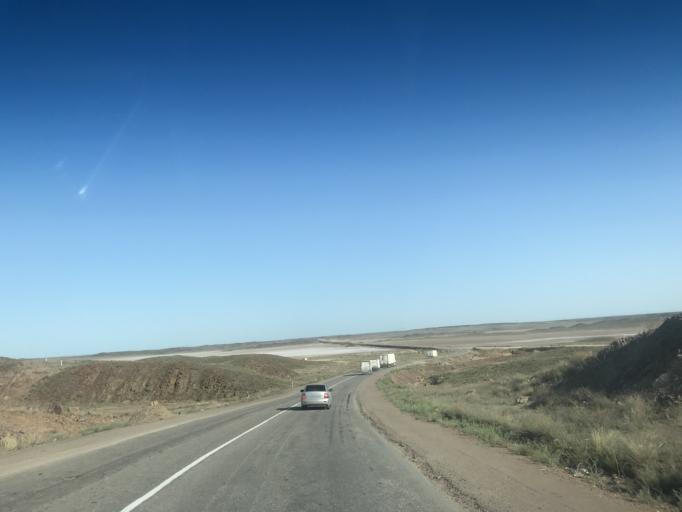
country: KZ
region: Zhambyl
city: Mynaral
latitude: 45.3238
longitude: 73.7391
